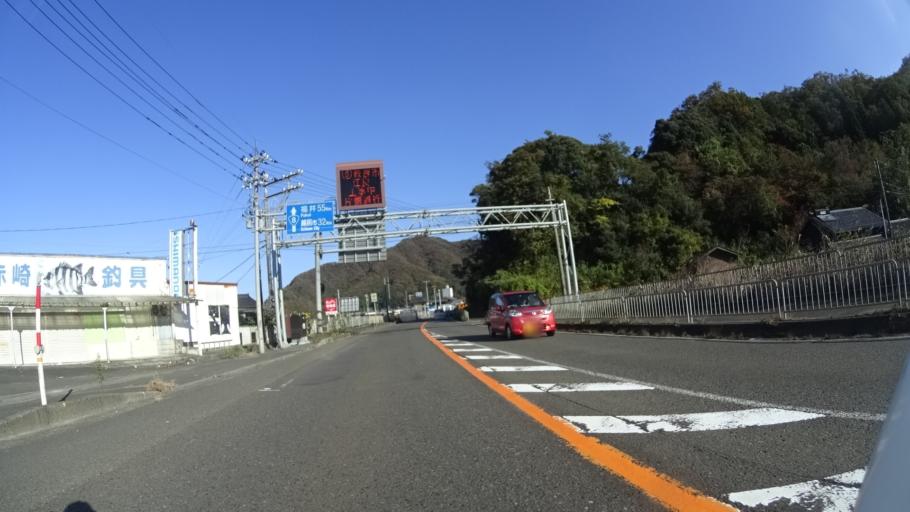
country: JP
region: Fukui
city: Tsuruga
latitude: 35.6805
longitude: 136.0854
